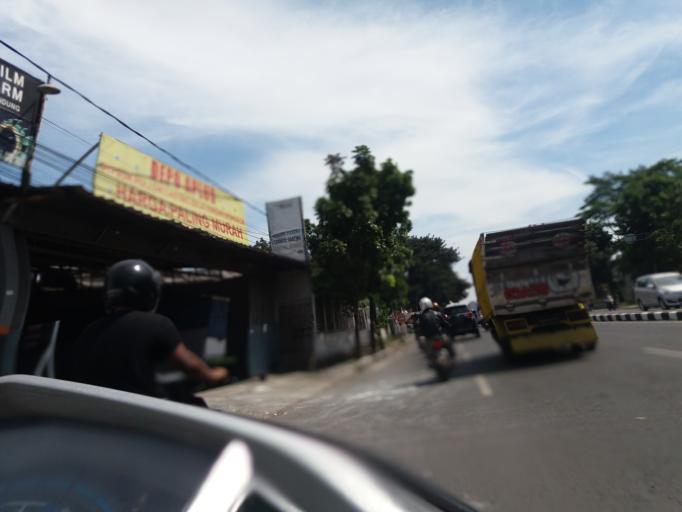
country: ID
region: West Java
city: Margahayukencana
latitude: -6.9478
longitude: 107.6006
